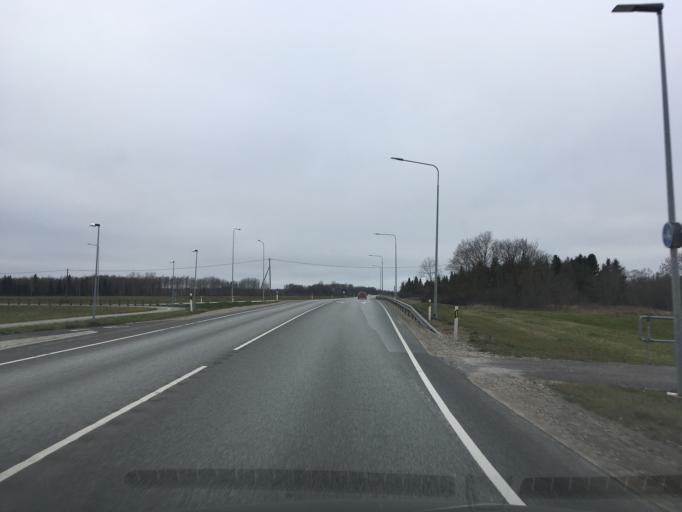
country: EE
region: Ida-Virumaa
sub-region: Narva-Joesuu linn
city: Narva-Joesuu
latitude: 59.3910
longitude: 28.0943
